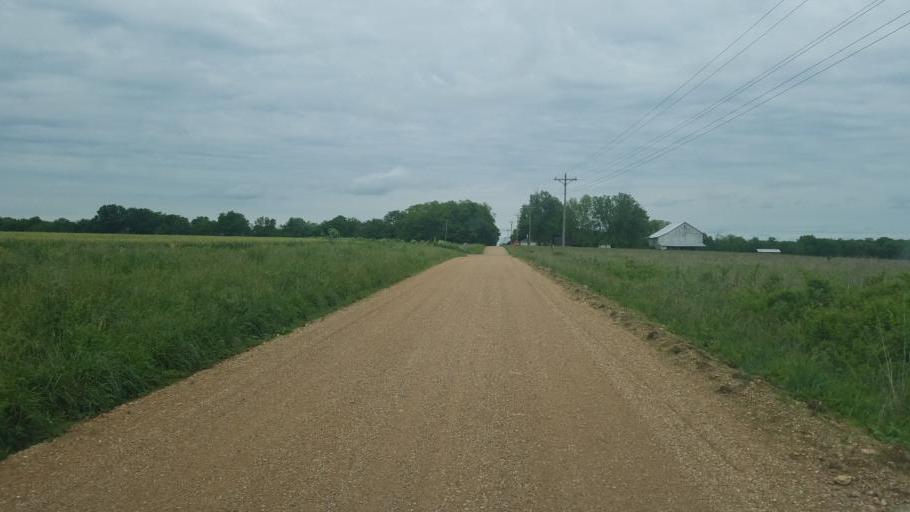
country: US
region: Missouri
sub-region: Morgan County
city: Versailles
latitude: 38.5061
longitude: -92.7898
